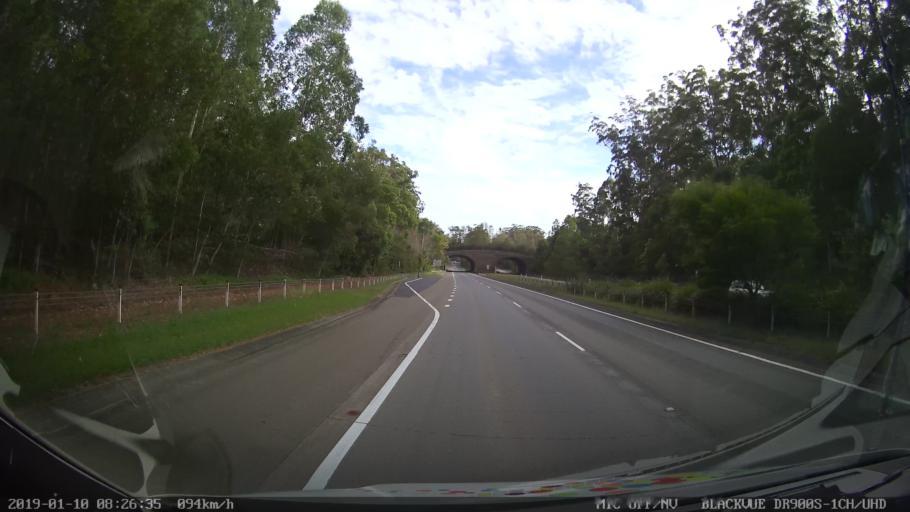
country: AU
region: New South Wales
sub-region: Coffs Harbour
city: Bonville
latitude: -30.4189
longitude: 153.0245
